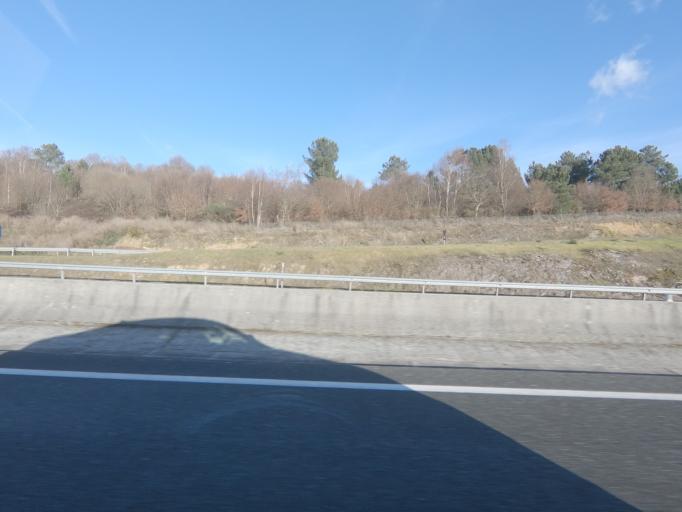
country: ES
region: Galicia
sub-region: Provincia de Pontevedra
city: Lalin
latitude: 42.6403
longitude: -8.1325
